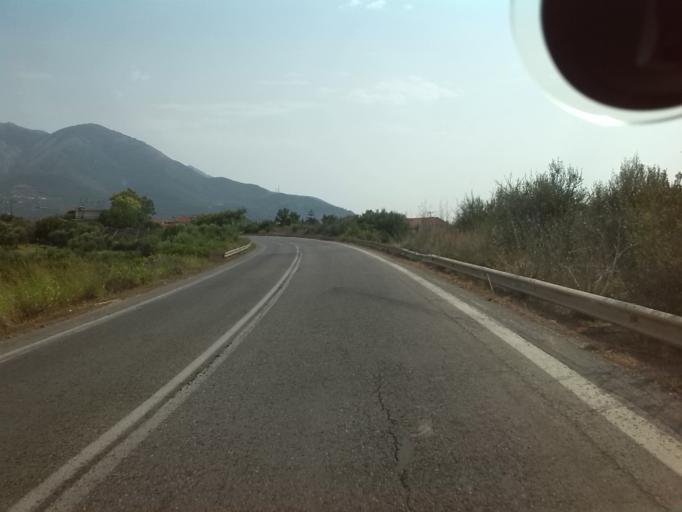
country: GR
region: Peloponnese
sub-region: Nomos Messinias
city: Kyparissia
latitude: 37.2801
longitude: 21.6990
